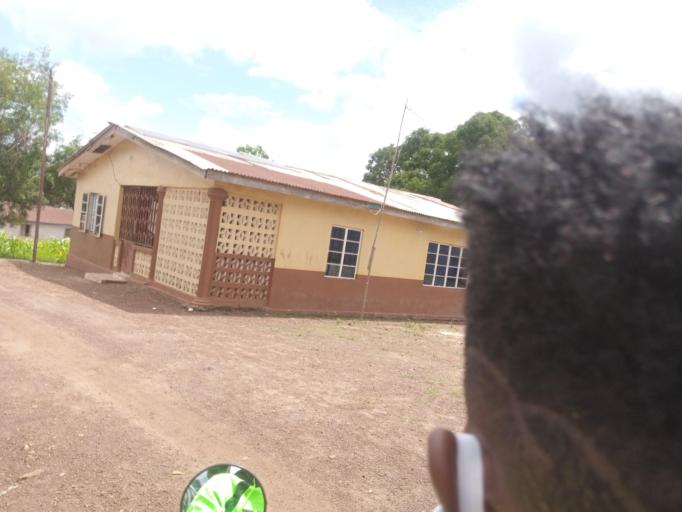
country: SL
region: Northern Province
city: Port Loko
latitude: 8.7600
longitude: -12.7805
